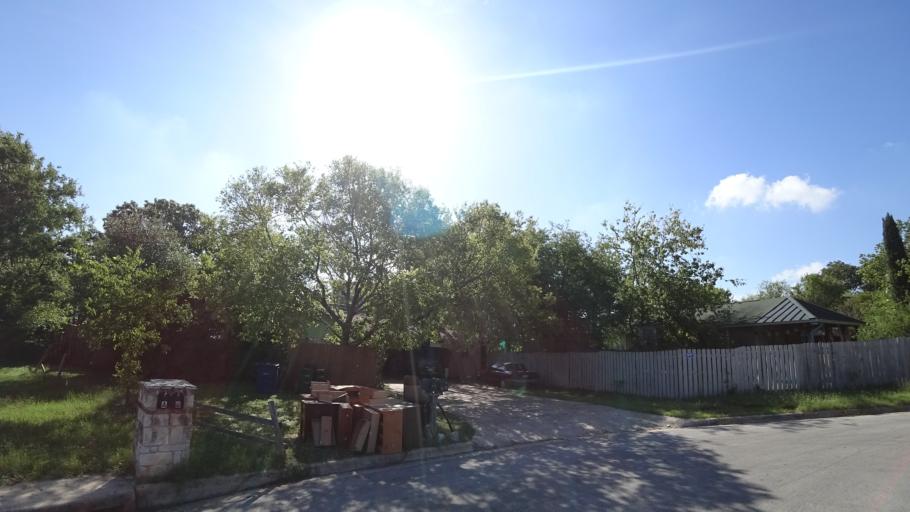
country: US
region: Texas
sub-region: Travis County
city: Austin
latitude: 30.3417
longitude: -97.7056
